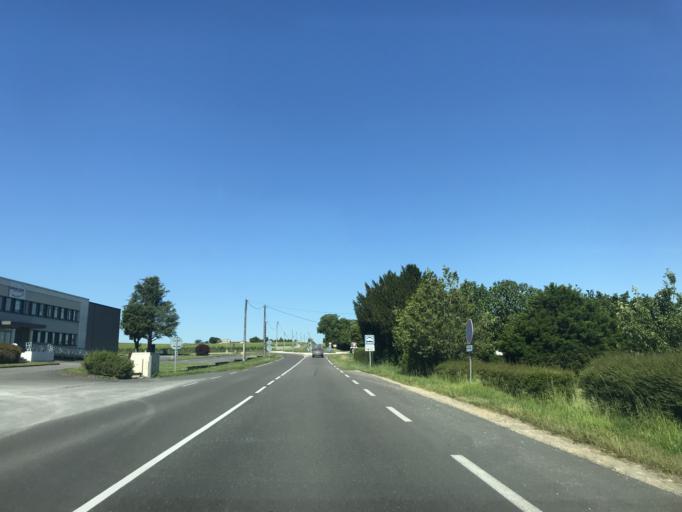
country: FR
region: Poitou-Charentes
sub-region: Departement de la Charente
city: Barbezieux-Saint-Hilaire
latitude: 45.4933
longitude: -0.2023
